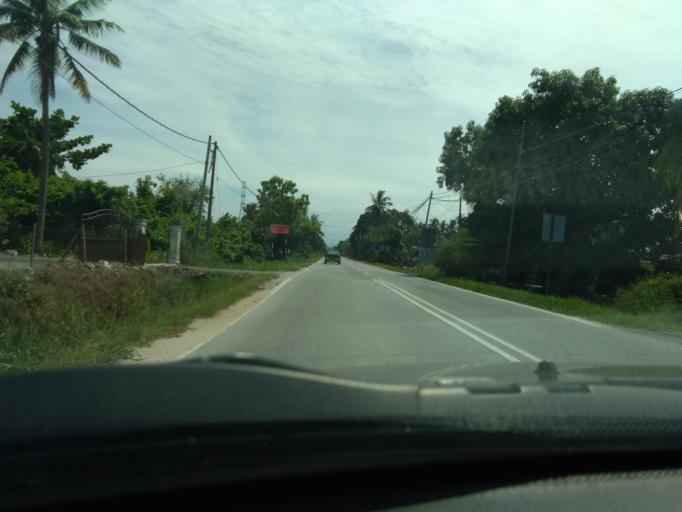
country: MY
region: Perak
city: Bagan Serai
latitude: 5.0150
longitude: 100.5400
